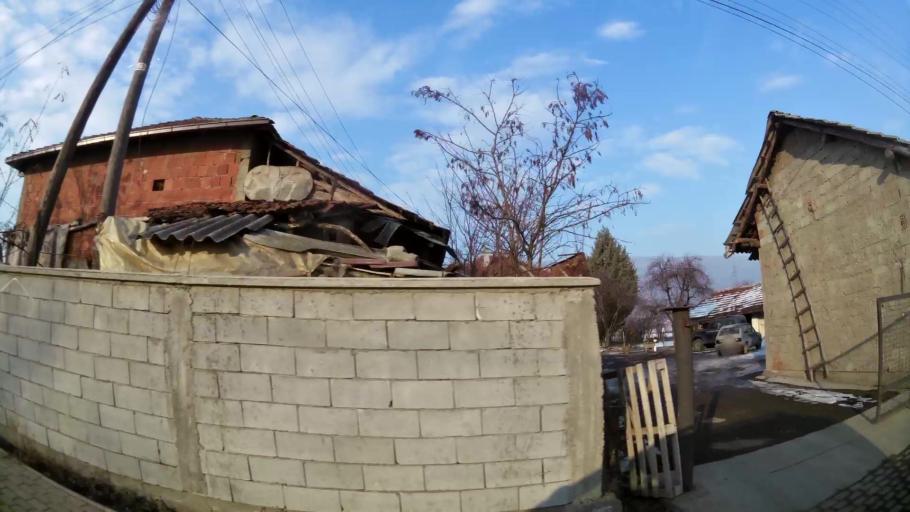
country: MK
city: Creshevo
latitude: 42.0269
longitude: 21.5267
